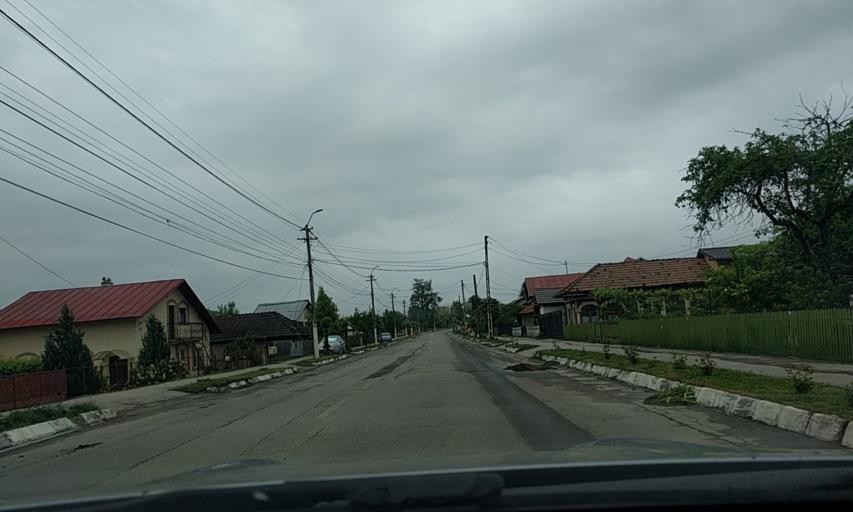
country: RO
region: Dambovita
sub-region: Oras Pucioasa
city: Glodeni
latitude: 45.0471
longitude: 25.4379
